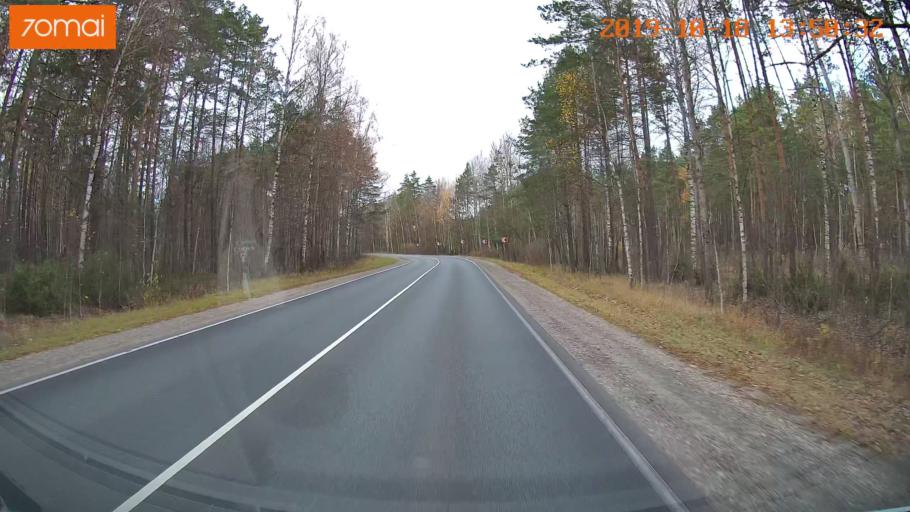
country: RU
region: Moskovskaya
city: Radovitskiy
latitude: 55.0075
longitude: 39.9701
